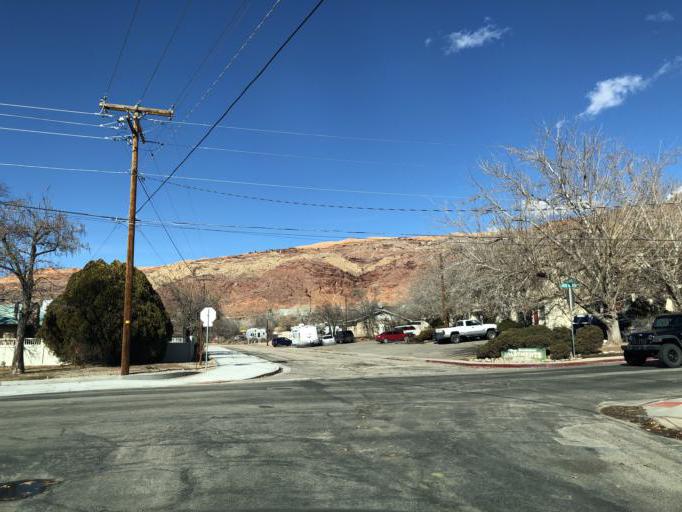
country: US
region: Utah
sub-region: Grand County
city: Moab
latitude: 38.5793
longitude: -109.5527
